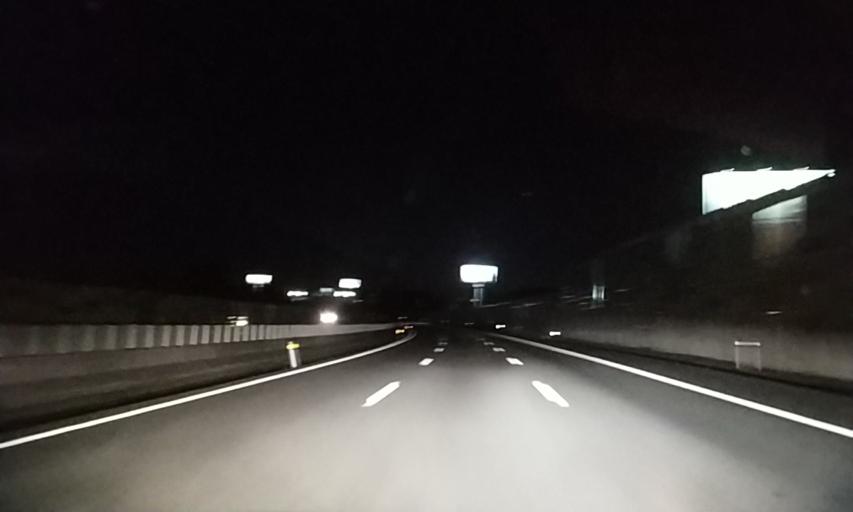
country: PT
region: Aveiro
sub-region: Santa Maria da Feira
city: Pacos de Brandao
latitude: 40.9806
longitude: -8.5769
